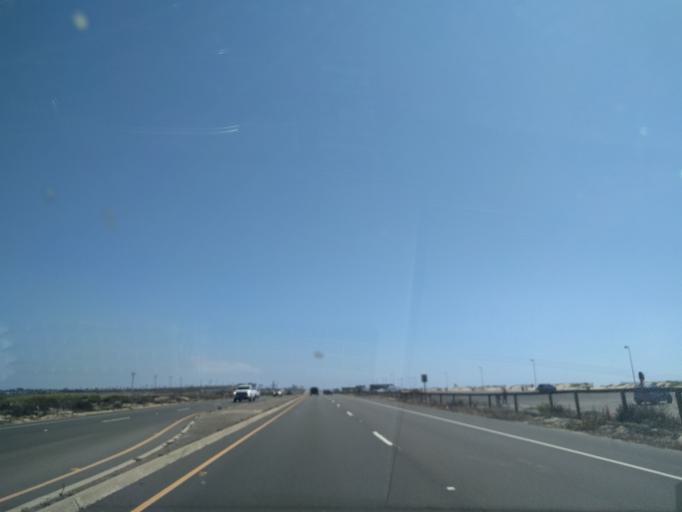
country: US
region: California
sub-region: Orange County
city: Huntington Beach
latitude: 33.6906
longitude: -118.0425
